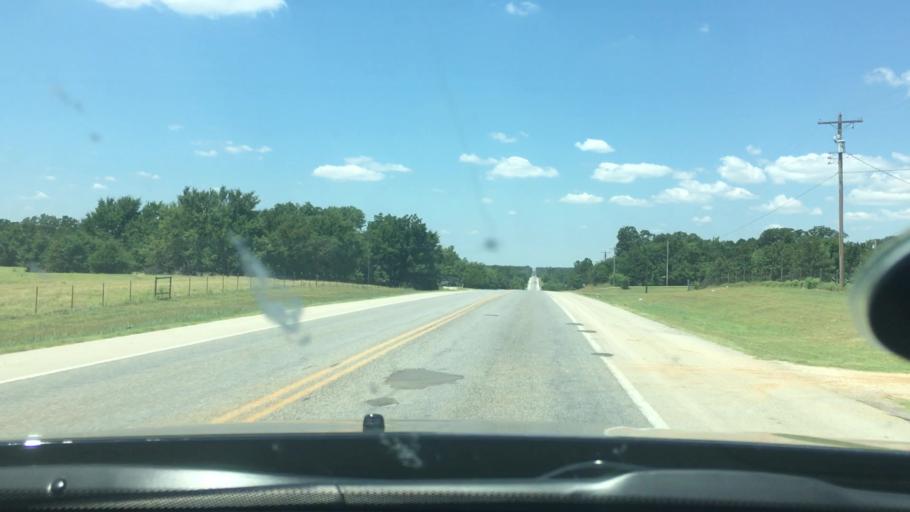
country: US
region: Oklahoma
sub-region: Carter County
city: Dickson
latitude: 34.1873
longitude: -96.9112
